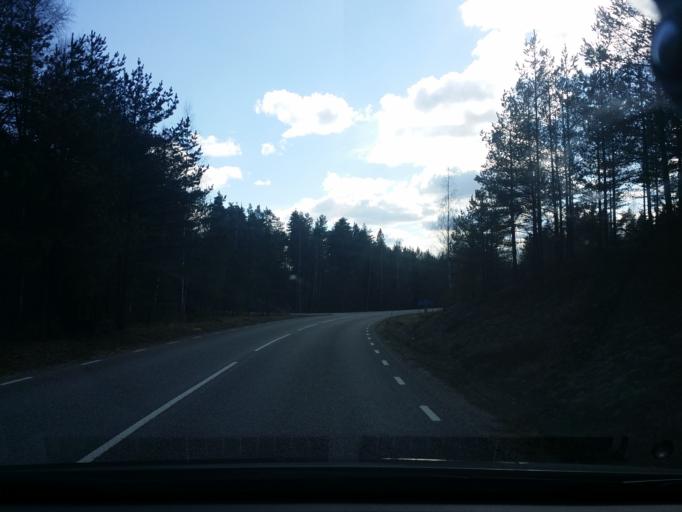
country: SE
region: Vaestmanland
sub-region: Sala Kommun
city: Sala
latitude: 59.9926
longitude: 16.4839
